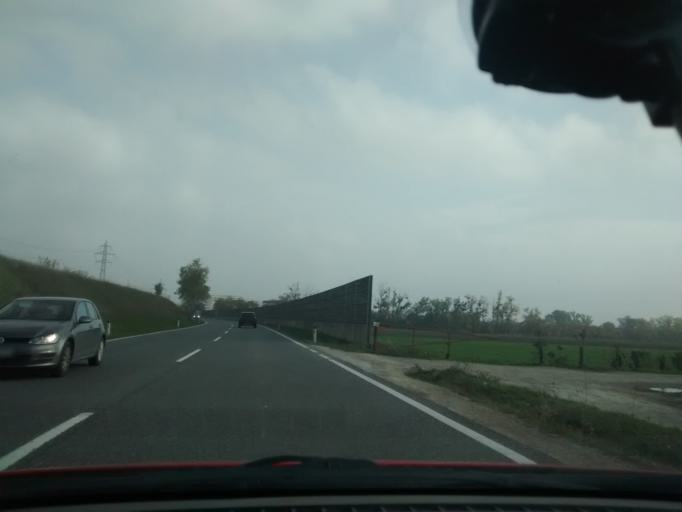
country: AT
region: Lower Austria
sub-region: Politischer Bezirk Modling
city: Biedermannsdorf
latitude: 48.0779
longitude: 16.3444
